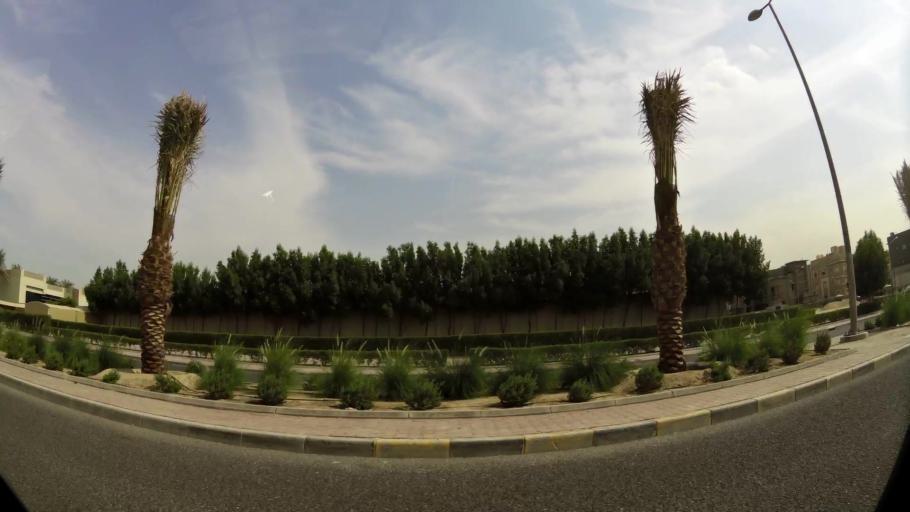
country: KW
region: Al Farwaniyah
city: Janub as Surrah
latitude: 29.2960
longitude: 47.9972
